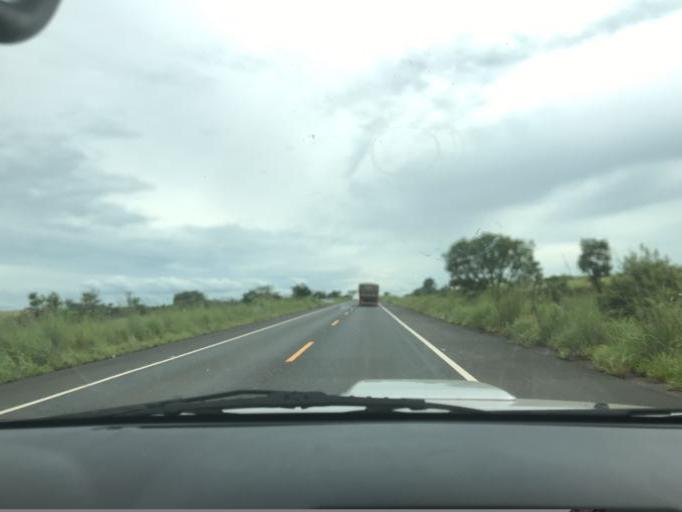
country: BR
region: Minas Gerais
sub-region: Araxa
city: Araxa
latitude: -19.3791
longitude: -46.8588
